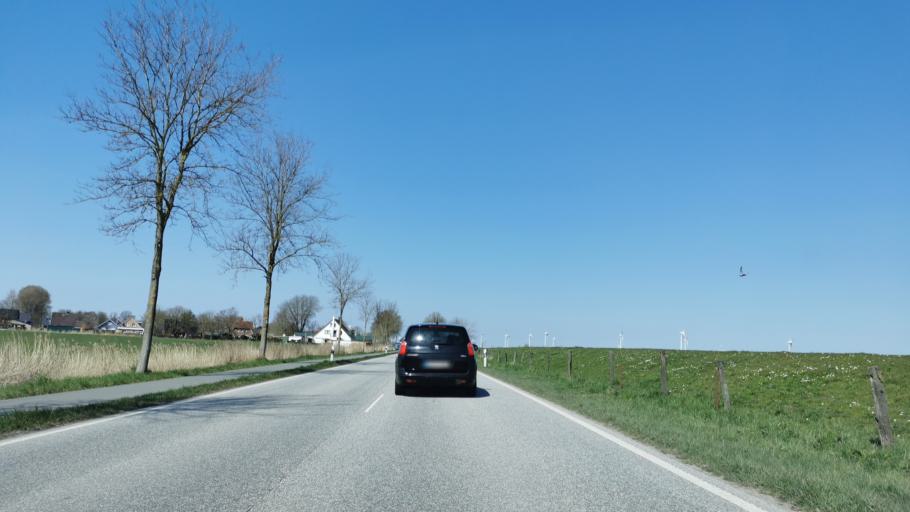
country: DE
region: Schleswig-Holstein
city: Wesselburener Deichhausen
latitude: 54.1559
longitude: 8.9109
